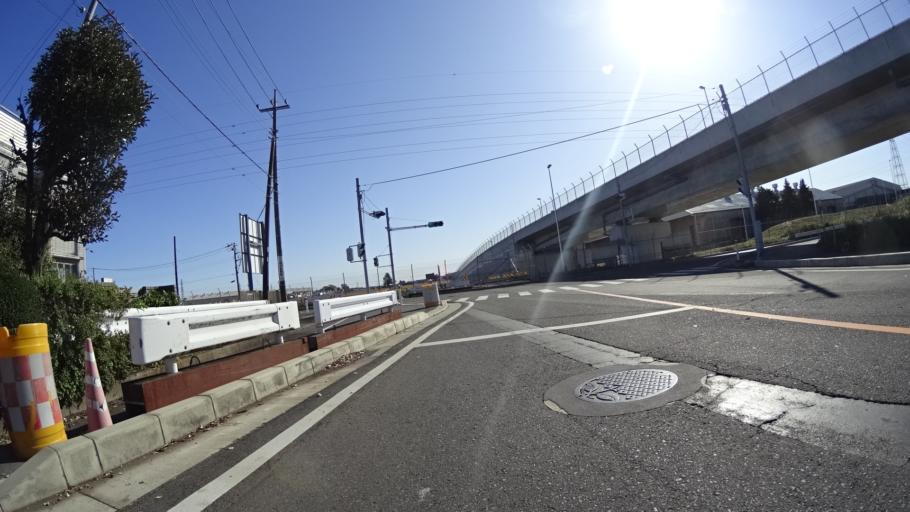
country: JP
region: Tokyo
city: Hachioji
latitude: 35.5883
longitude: 139.3771
